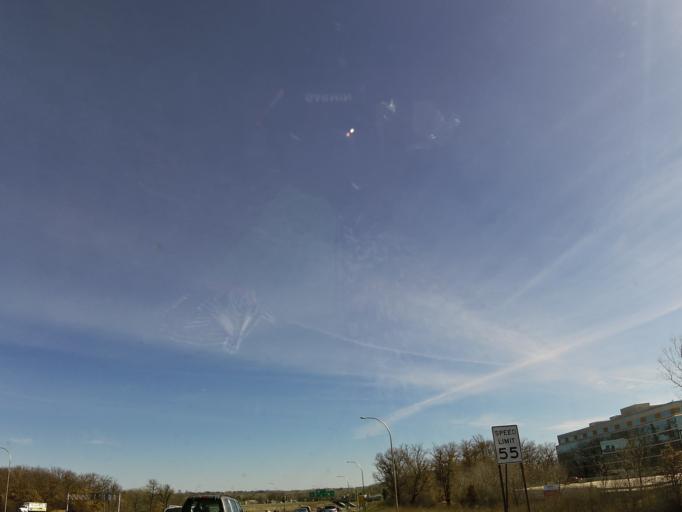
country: US
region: Minnesota
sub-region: Hennepin County
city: Edina
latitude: 44.8890
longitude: -93.4056
